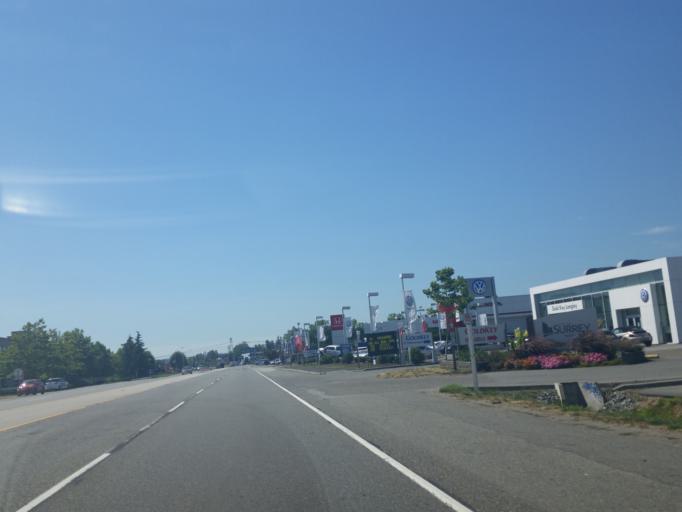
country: CA
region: British Columbia
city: Langley
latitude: 49.1096
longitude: -122.6806
